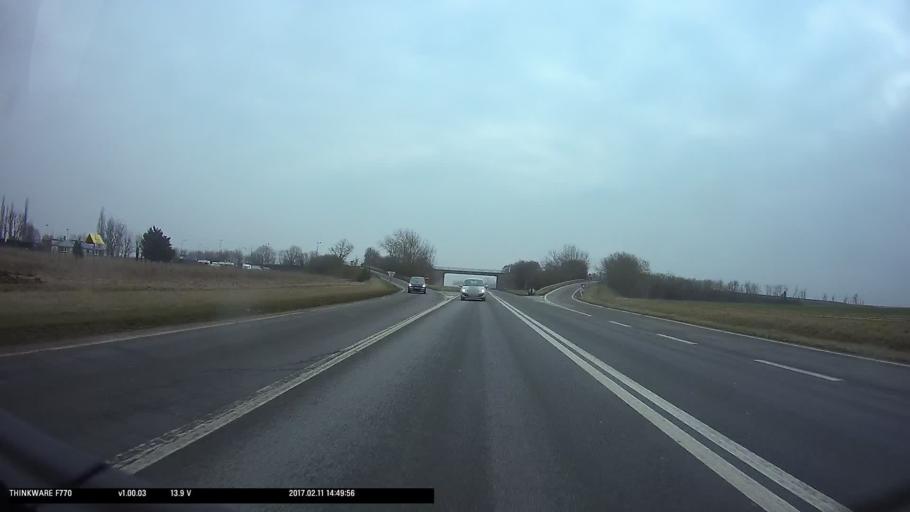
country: FR
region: Ile-de-France
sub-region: Departement des Yvelines
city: Ablis
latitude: 48.5125
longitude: 1.8288
